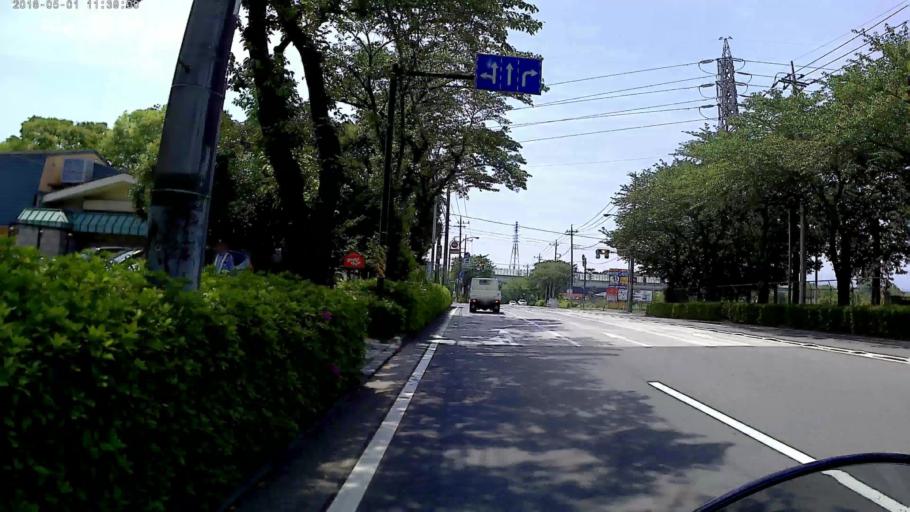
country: JP
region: Kanagawa
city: Minami-rinkan
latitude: 35.5058
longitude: 139.4896
